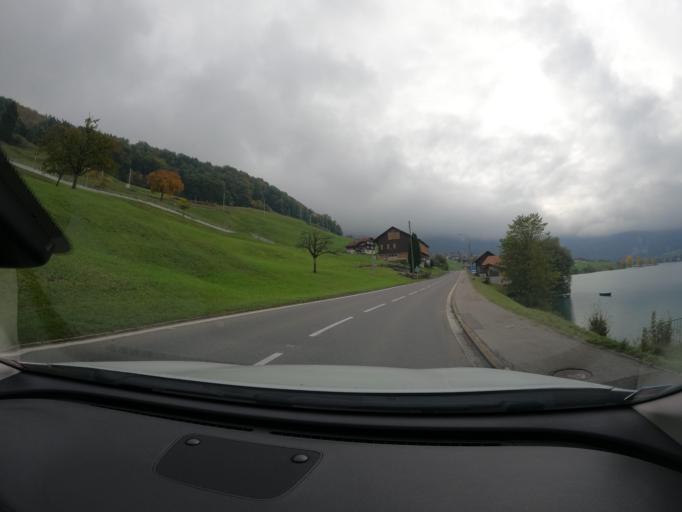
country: CH
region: Obwalden
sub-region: Obwalden
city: Lungern
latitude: 46.7953
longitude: 8.1642
